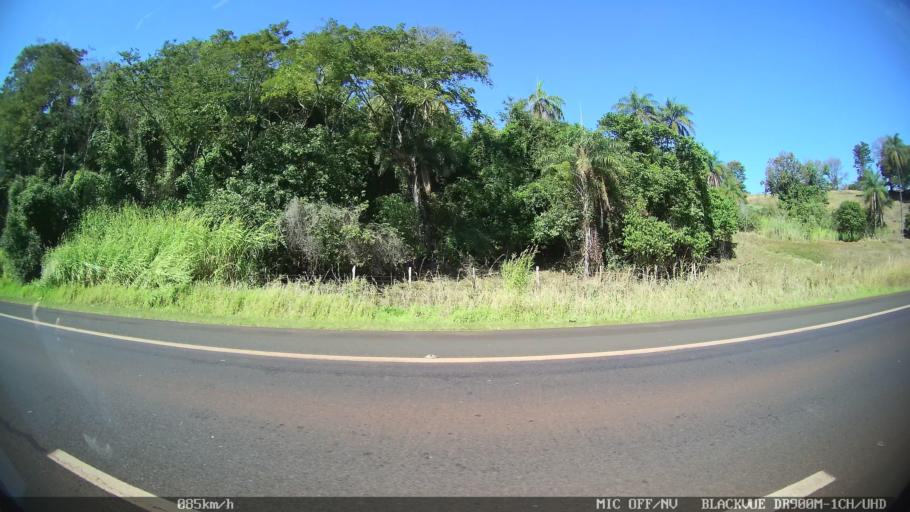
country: BR
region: Sao Paulo
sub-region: Franca
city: Franca
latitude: -20.6043
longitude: -47.4482
